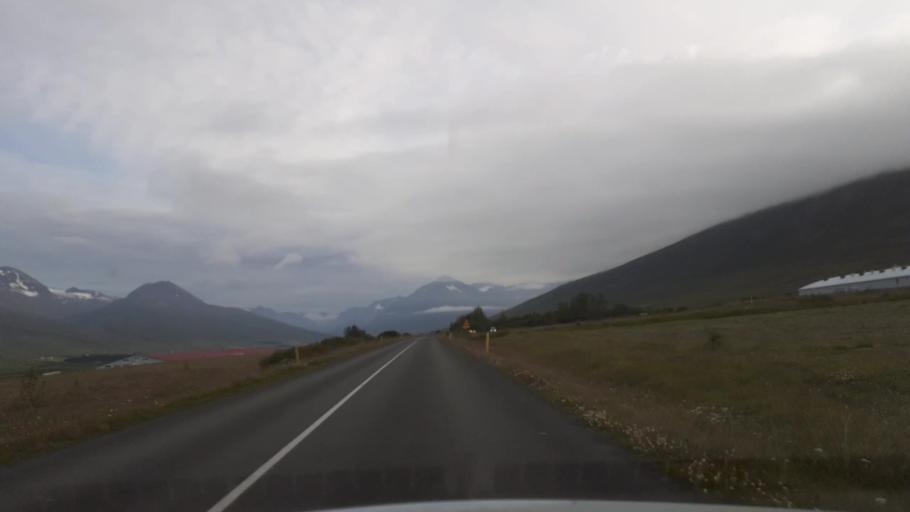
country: IS
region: Northeast
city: Dalvik
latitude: 65.9535
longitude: -18.5519
